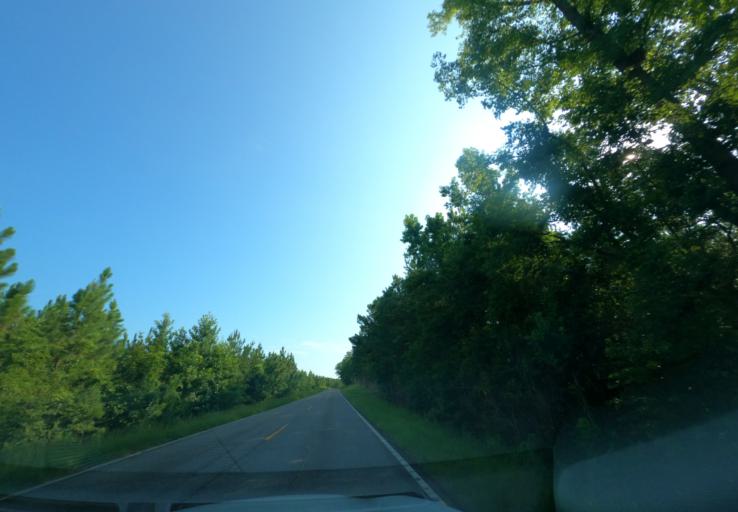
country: US
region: South Carolina
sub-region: Edgefield County
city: Edgefield
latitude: 33.7526
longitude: -81.9571
